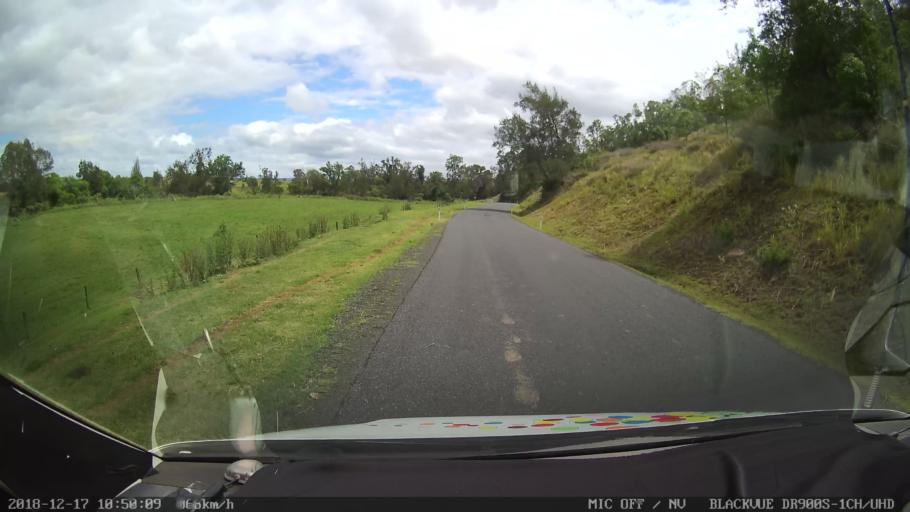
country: AU
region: New South Wales
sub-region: Clarence Valley
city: Gordon
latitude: -28.8617
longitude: 152.5742
